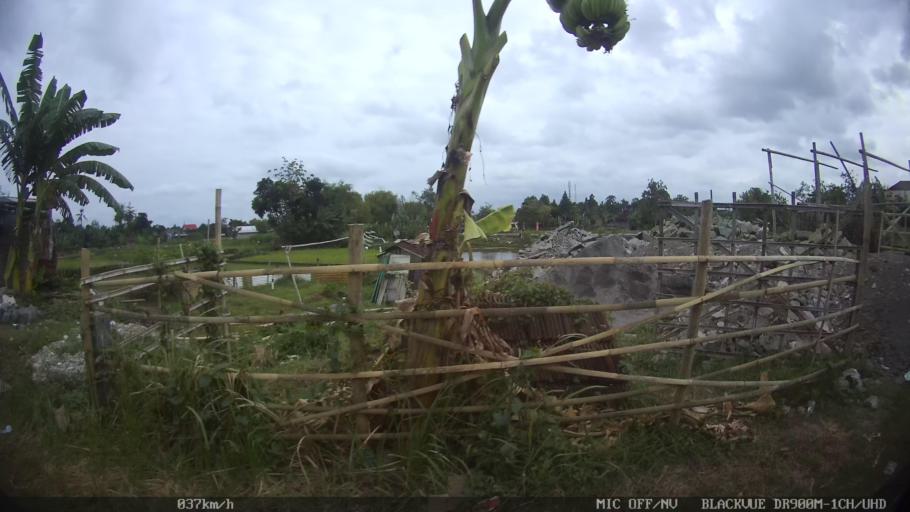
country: ID
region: Daerah Istimewa Yogyakarta
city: Depok
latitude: -7.8344
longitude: 110.4211
